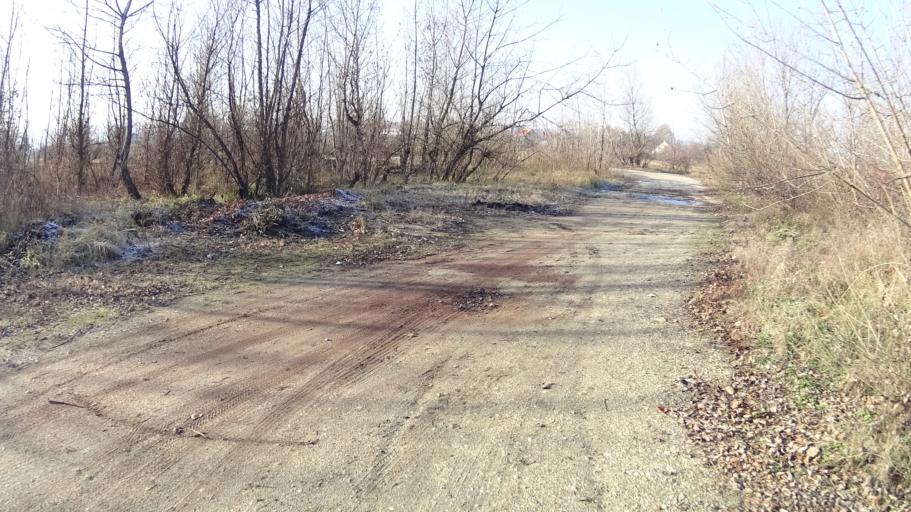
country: HU
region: Borsod-Abauj-Zemplen
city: Nyekladhaza
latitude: 47.9880
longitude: 20.8486
